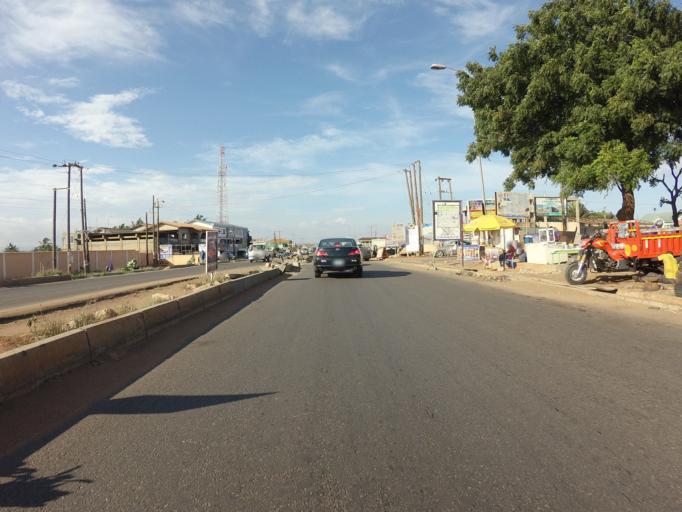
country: GH
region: Greater Accra
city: Nungua
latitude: 5.6420
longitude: -0.0607
